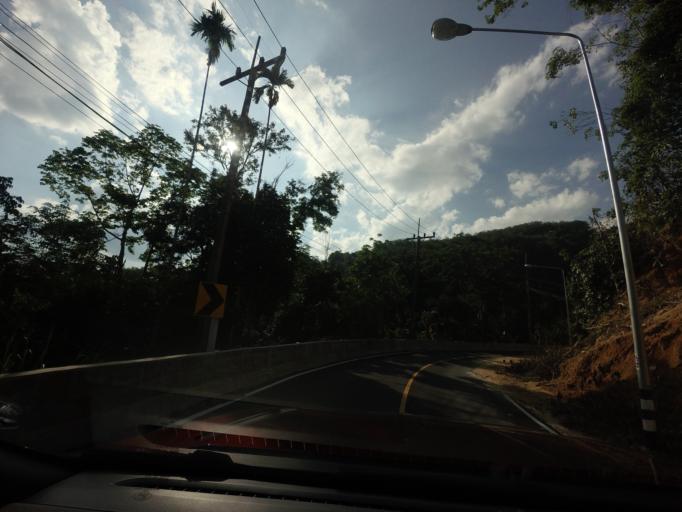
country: TH
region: Yala
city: Than To
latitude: 6.1324
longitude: 101.2982
